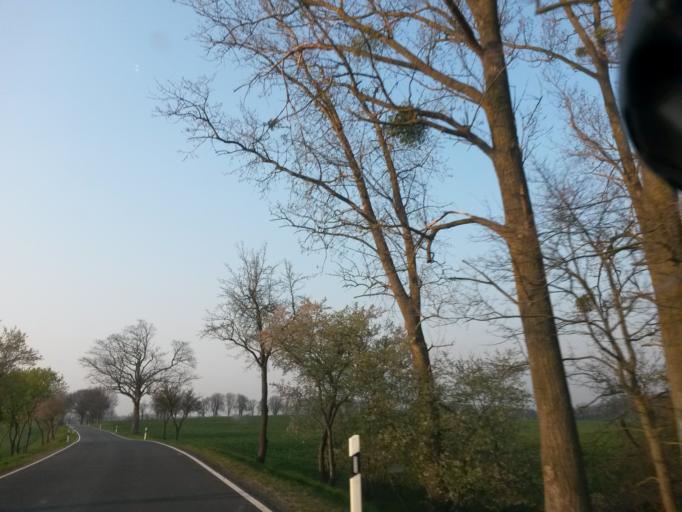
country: DE
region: Brandenburg
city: Buckow
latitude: 52.6255
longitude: 14.0694
